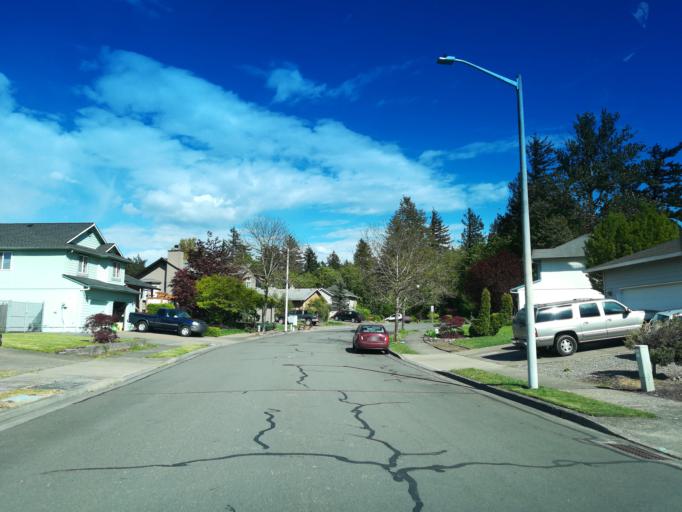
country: US
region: Oregon
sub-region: Multnomah County
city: Troutdale
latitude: 45.5340
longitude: -122.3820
